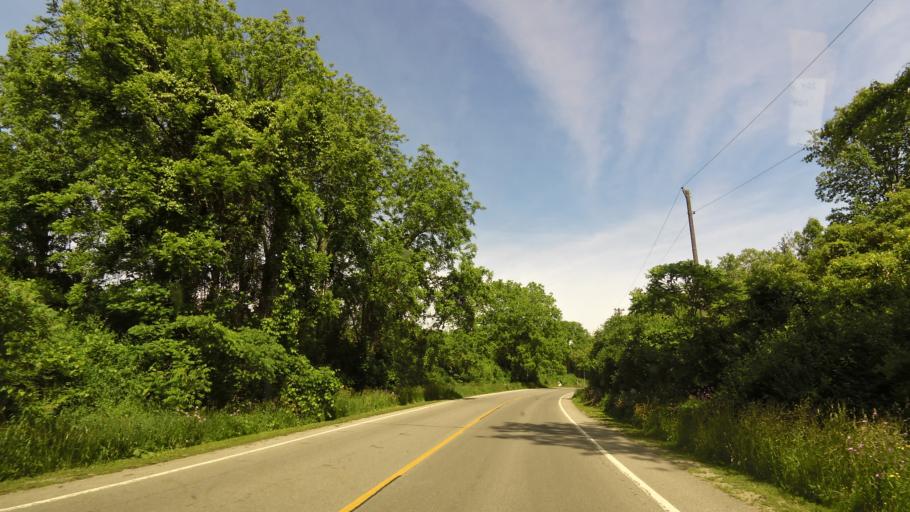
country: CA
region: Ontario
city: Norfolk County
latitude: 42.6789
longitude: -80.3716
